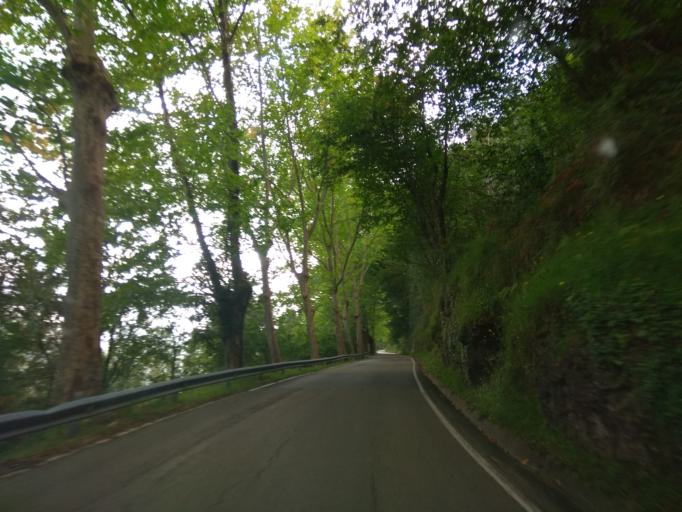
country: ES
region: Cantabria
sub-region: Provincia de Cantabria
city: San Vicente de la Barquera
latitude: 43.3226
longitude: -4.3695
